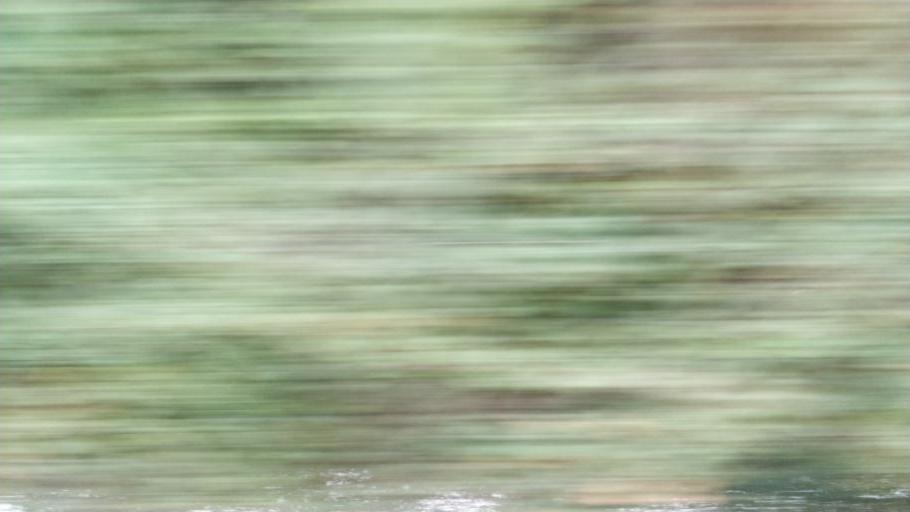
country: GB
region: England
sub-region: Lancashire
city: Parbold
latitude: 53.5866
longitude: -2.7540
